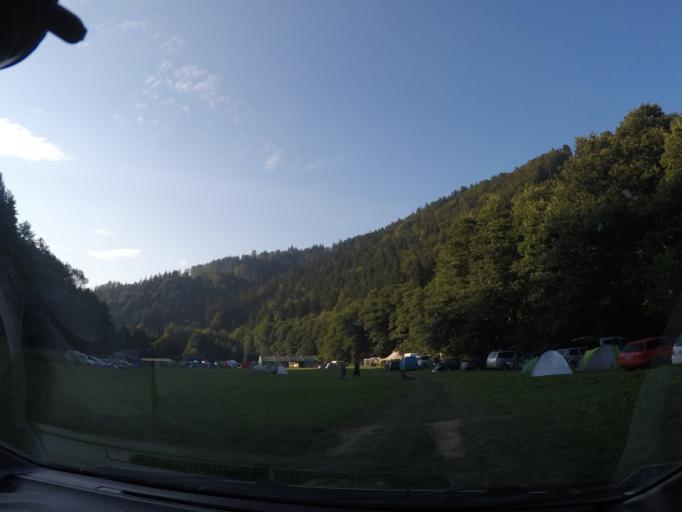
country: SK
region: Nitriansky
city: Bojnice
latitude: 48.9078
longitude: 18.6030
